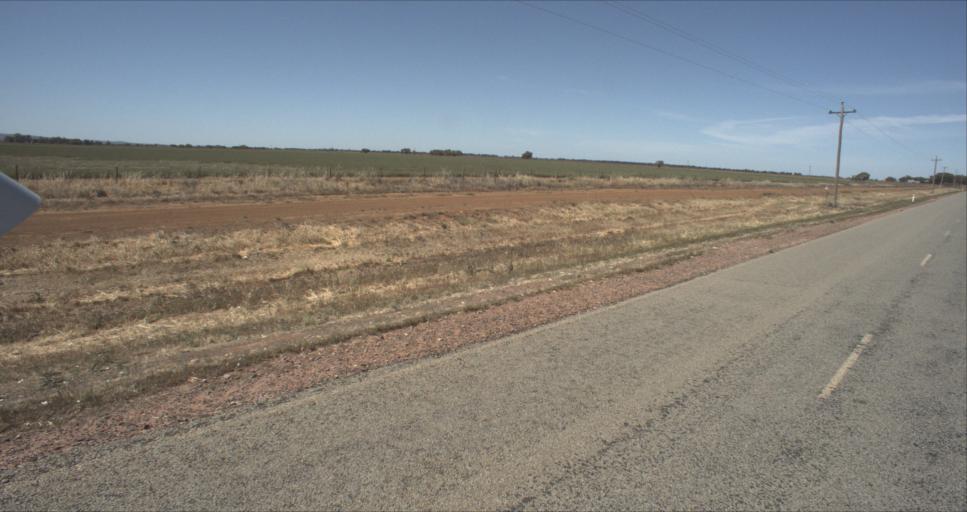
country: AU
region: New South Wales
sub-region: Leeton
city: Leeton
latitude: -34.4533
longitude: 146.2956
